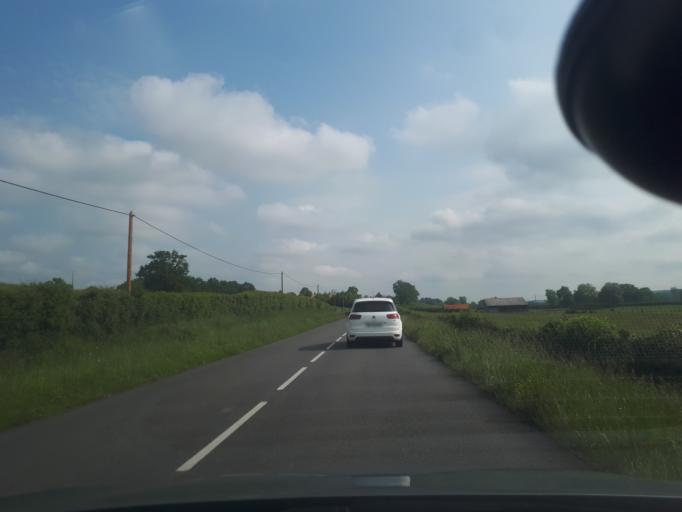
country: FR
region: Auvergne
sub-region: Departement de l'Allier
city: Lapalisse
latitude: 46.3998
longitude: 3.5981
